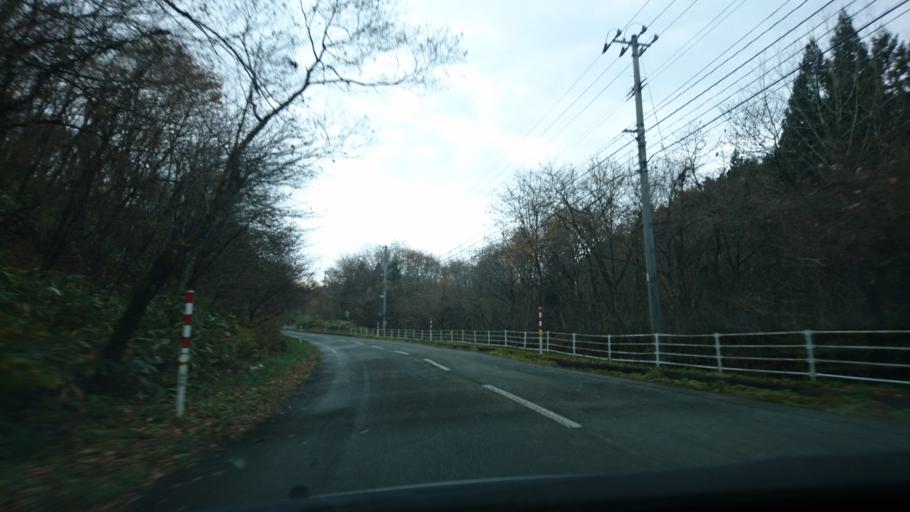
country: JP
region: Iwate
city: Ichinoseki
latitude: 38.9674
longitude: 140.9385
